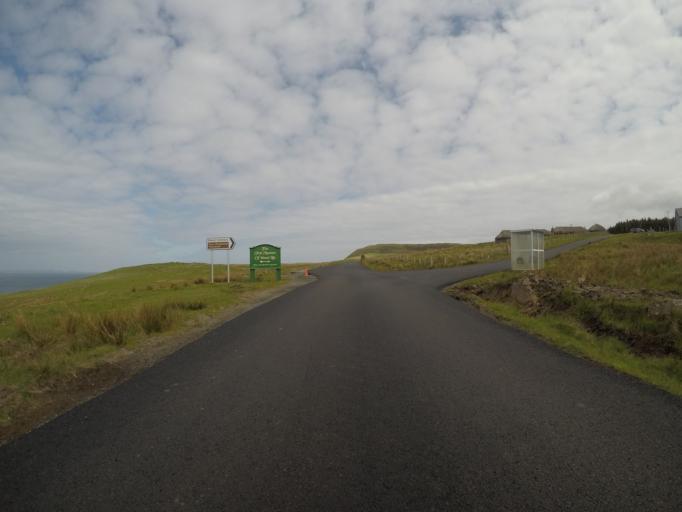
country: GB
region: Scotland
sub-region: Highland
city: Portree
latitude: 57.6603
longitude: -6.3711
